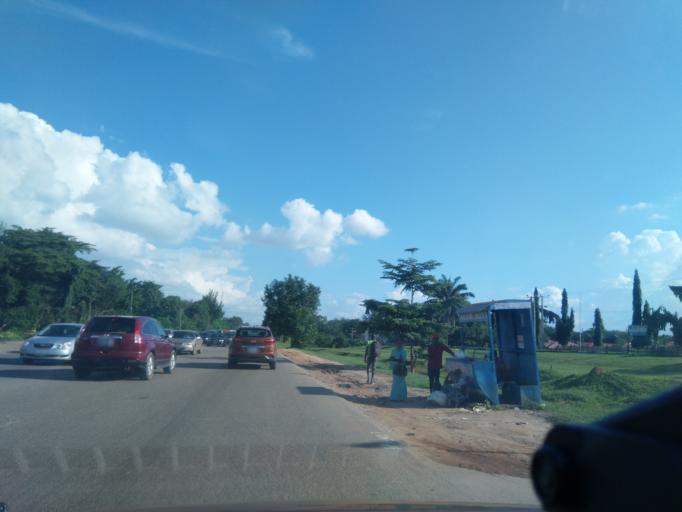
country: NG
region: Abuja Federal Capital Territory
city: Abuja
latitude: 9.0447
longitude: 7.4116
